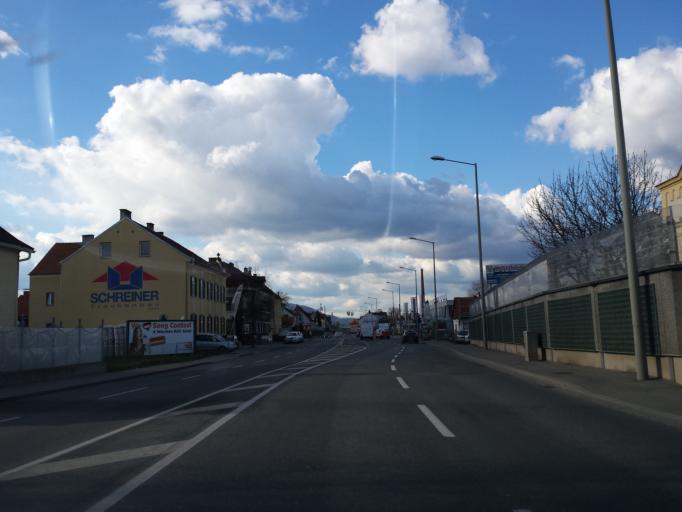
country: AT
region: Styria
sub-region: Politischer Bezirk Graz-Umgebung
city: Feldkirchen bei Graz
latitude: 47.0234
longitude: 15.4362
